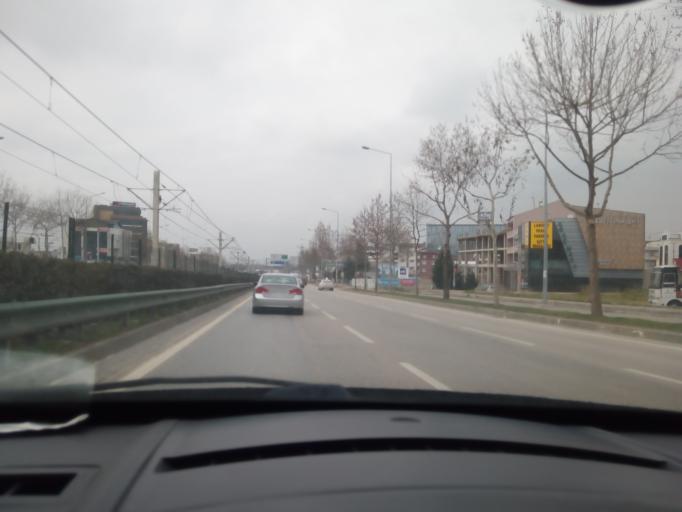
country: TR
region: Bursa
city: Yildirim
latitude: 40.2345
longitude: 28.9789
